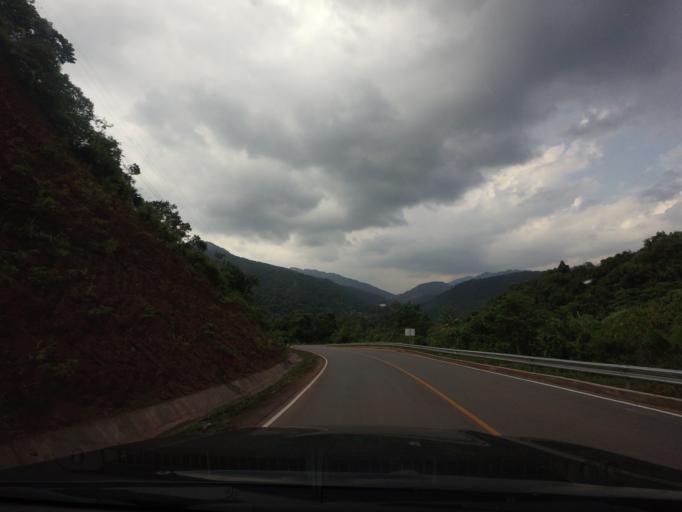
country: TH
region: Nan
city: Bo Kluea
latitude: 19.2646
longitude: 101.1785
